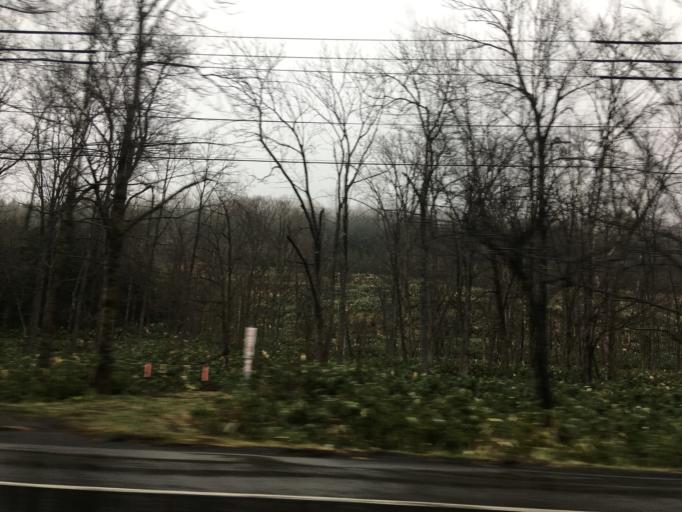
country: JP
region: Hokkaido
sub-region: Asahikawa-shi
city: Asahikawa
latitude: 43.9875
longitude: 142.4515
